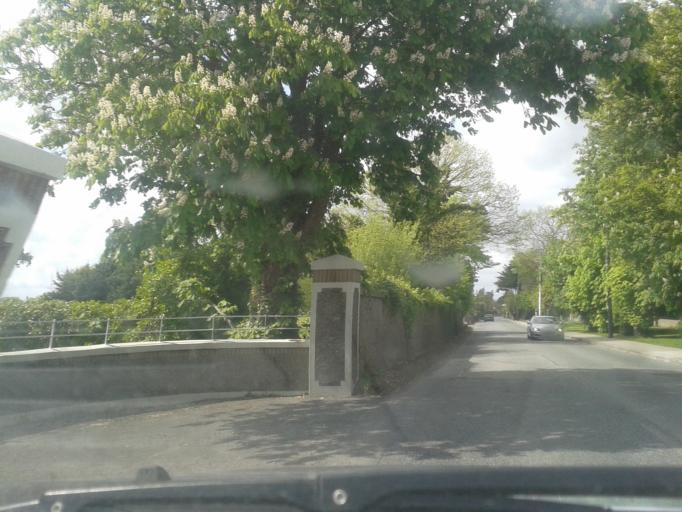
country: IE
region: Leinster
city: Cabinteely
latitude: 53.2774
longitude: -6.1539
